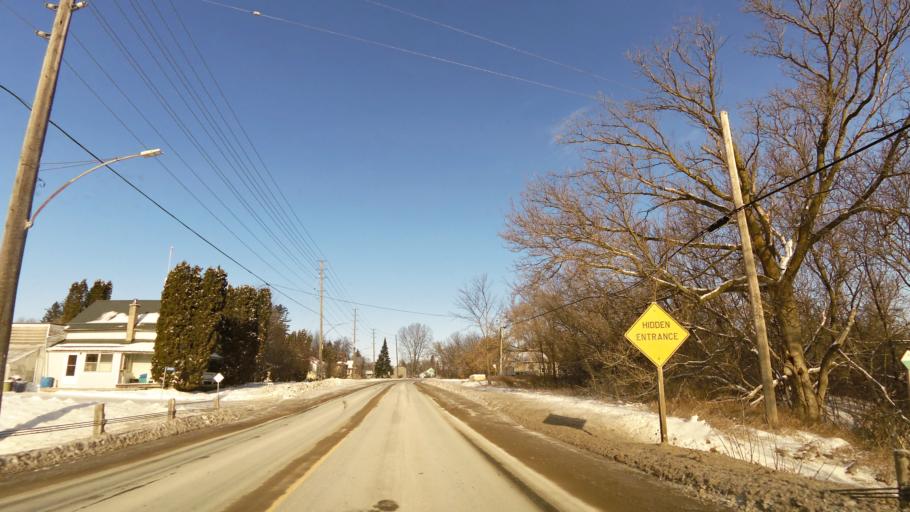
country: CA
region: Ontario
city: Quinte West
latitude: 44.1609
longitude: -77.8007
